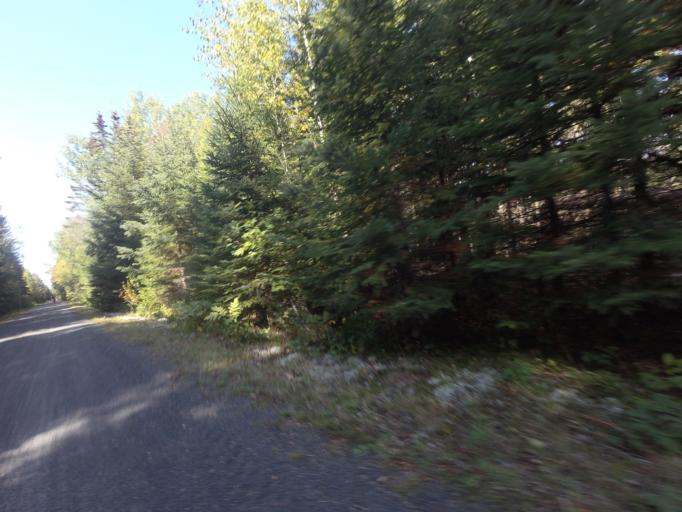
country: CA
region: Quebec
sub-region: Laurentides
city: Sainte-Agathe-des-Monts
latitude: 46.0962
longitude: -74.3567
